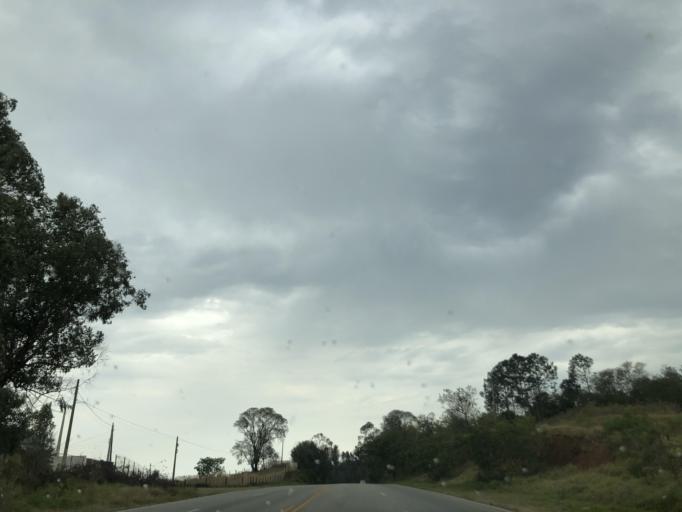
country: BR
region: Sao Paulo
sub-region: Salto De Pirapora
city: Salto de Pirapora
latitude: -23.6949
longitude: -47.6111
